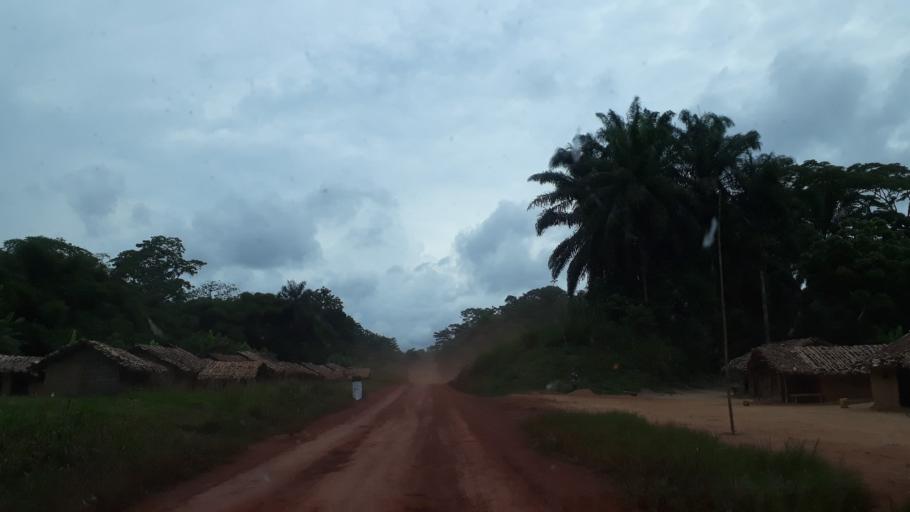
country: CD
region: Eastern Province
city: Kisangani
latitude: 0.5564
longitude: 25.8468
